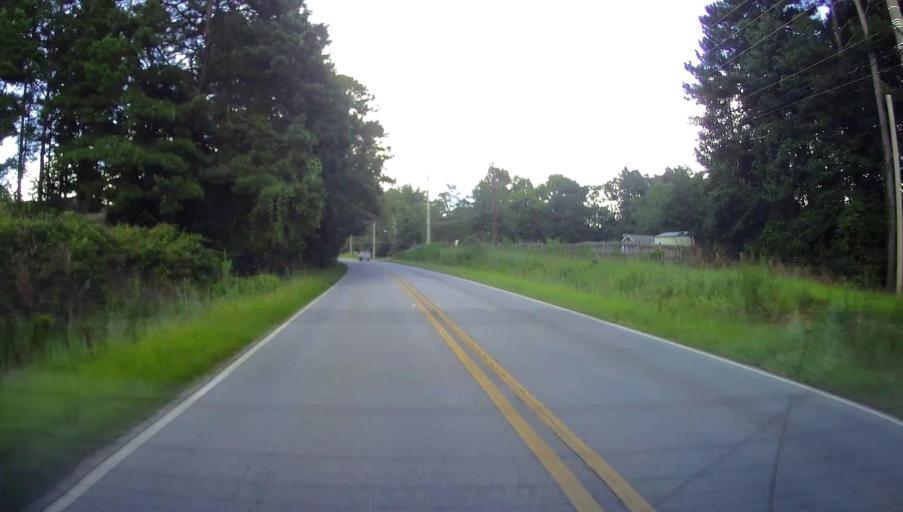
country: US
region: Georgia
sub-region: Muscogee County
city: Columbus
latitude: 32.5391
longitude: -84.8997
